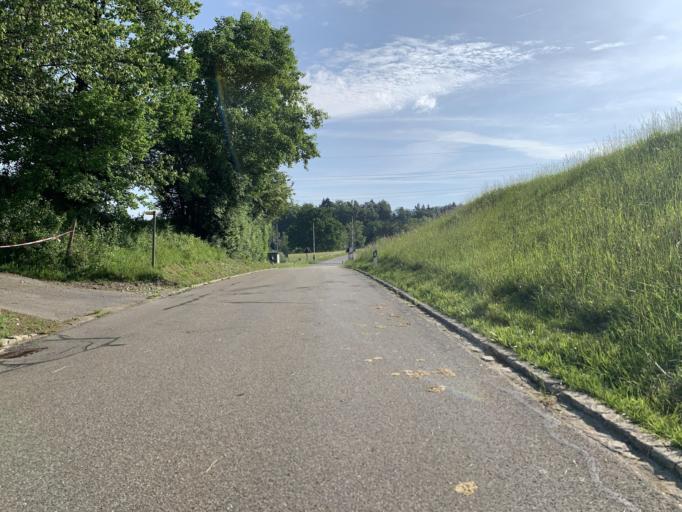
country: CH
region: Zurich
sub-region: Bezirk Hinwil
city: Wetzikon / Unter-Wetzikon
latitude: 47.2939
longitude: 8.8099
